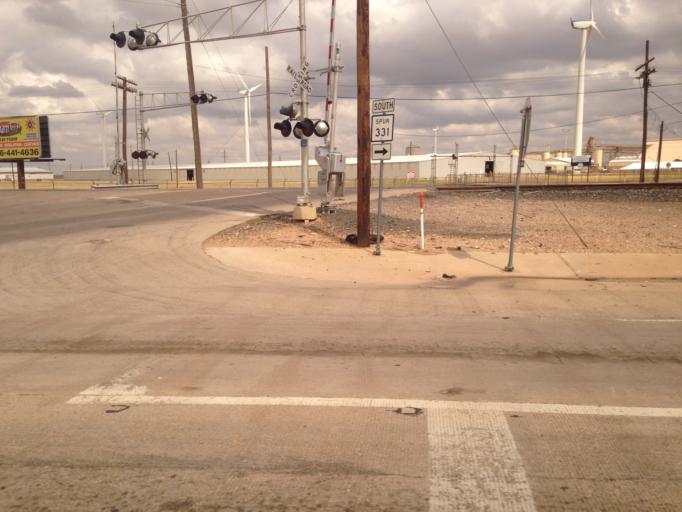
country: US
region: Texas
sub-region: Lubbock County
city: Lubbock
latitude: 33.5488
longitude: -101.8038
